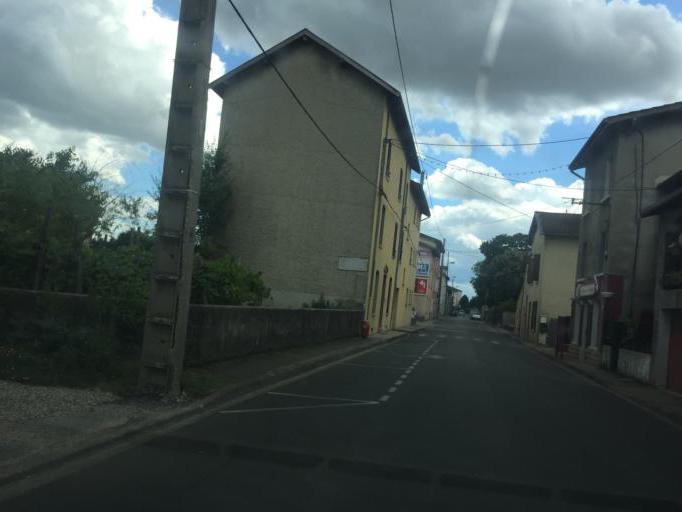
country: FR
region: Rhone-Alpes
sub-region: Departement de l'Isere
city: Pont-de-Cheruy
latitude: 45.7560
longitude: 5.1838
